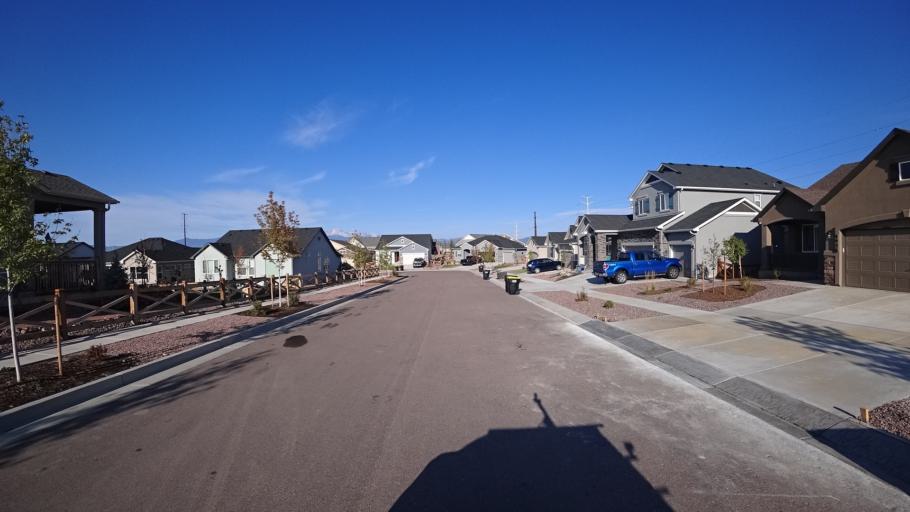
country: US
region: Colorado
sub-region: El Paso County
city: Black Forest
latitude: 38.9369
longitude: -104.6610
